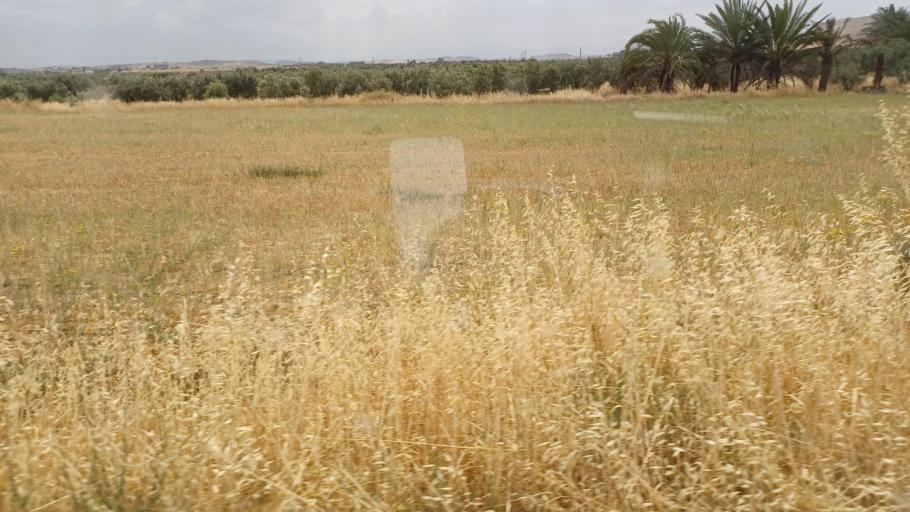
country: CY
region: Larnaka
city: Athienou
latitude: 35.0770
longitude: 33.5381
